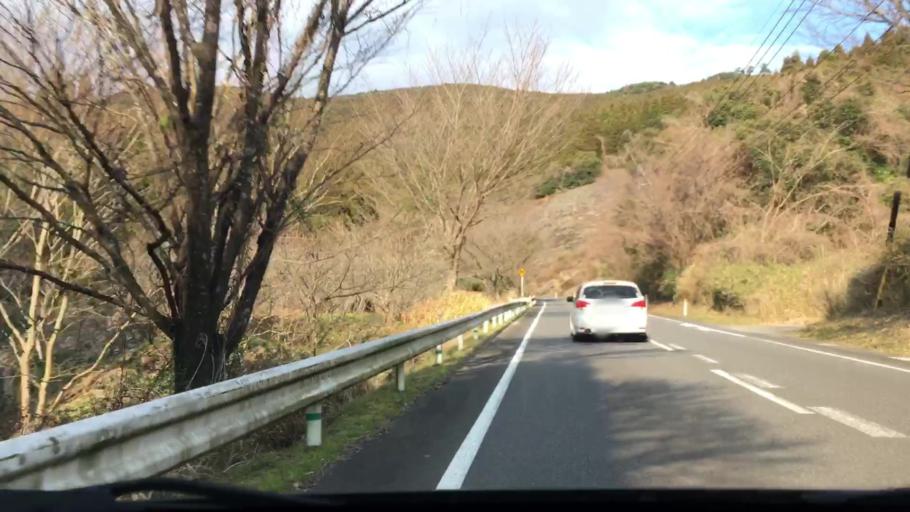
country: JP
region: Miyazaki
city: Miyazaki-shi
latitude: 31.7747
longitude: 131.3320
